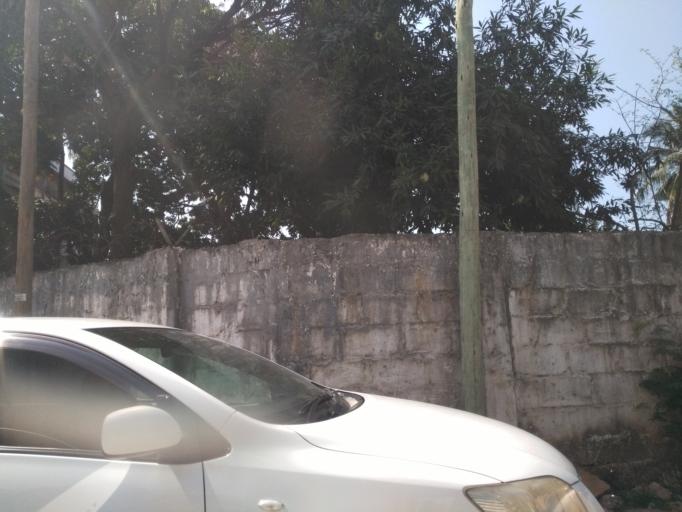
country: TZ
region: Dar es Salaam
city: Dar es Salaam
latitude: -6.8103
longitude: 39.2805
